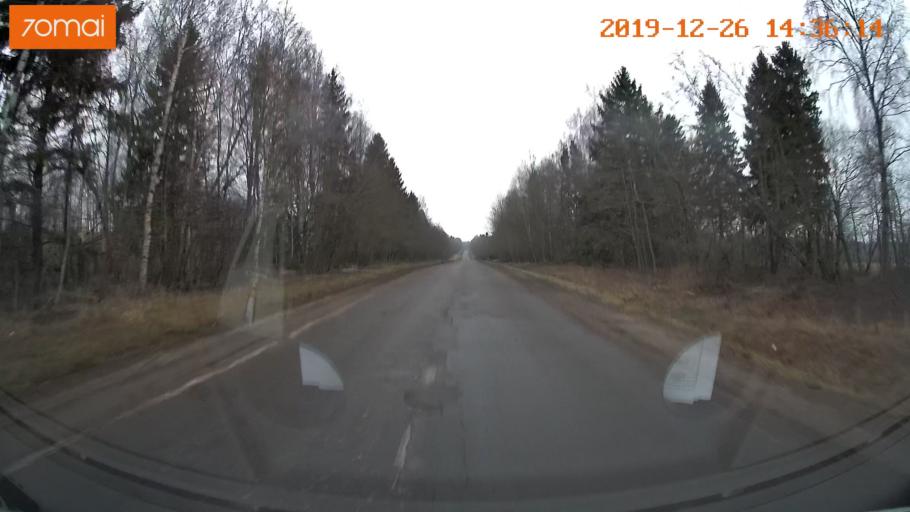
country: RU
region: Jaroslavl
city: Poshekhon'ye
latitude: 58.4132
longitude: 38.9769
